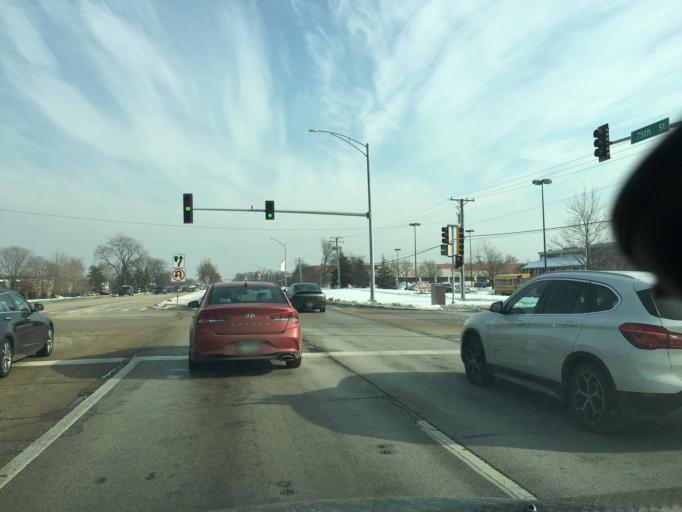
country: US
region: Illinois
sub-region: DuPage County
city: Darien
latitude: 41.7513
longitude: -88.0001
